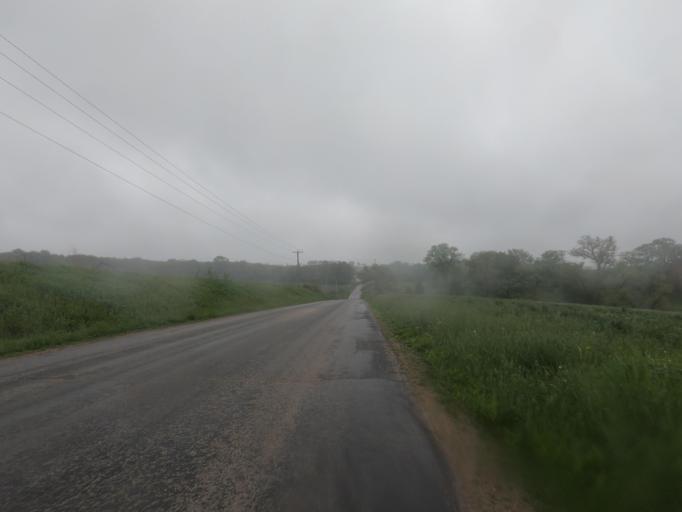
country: US
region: Wisconsin
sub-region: Grant County
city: Hazel Green
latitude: 42.5124
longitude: -90.5238
